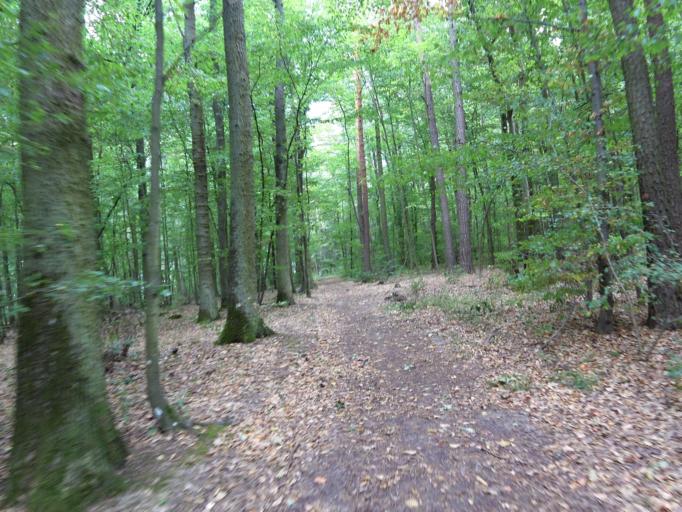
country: DE
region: Bavaria
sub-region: Regierungsbezirk Unterfranken
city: Gadheim
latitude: 49.8386
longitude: 9.8956
